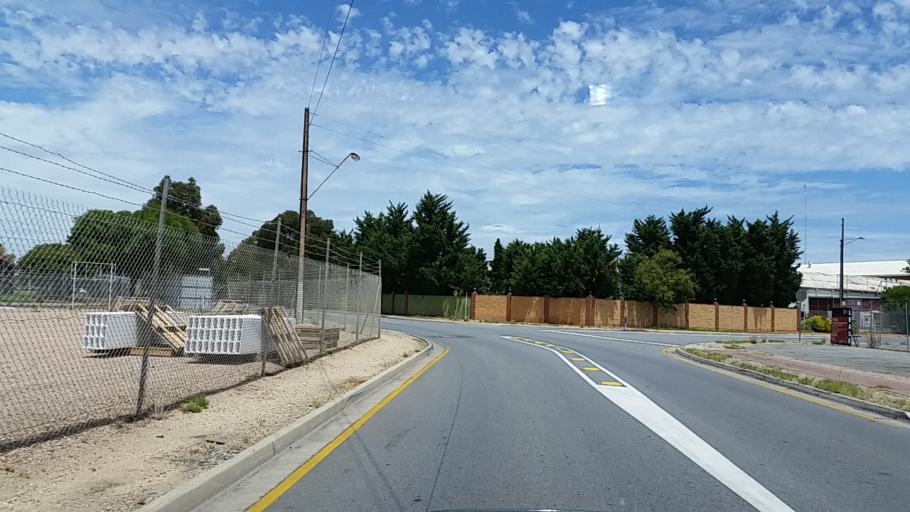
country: AU
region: South Australia
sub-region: Charles Sturt
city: Woodville North
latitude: -34.8652
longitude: 138.5384
